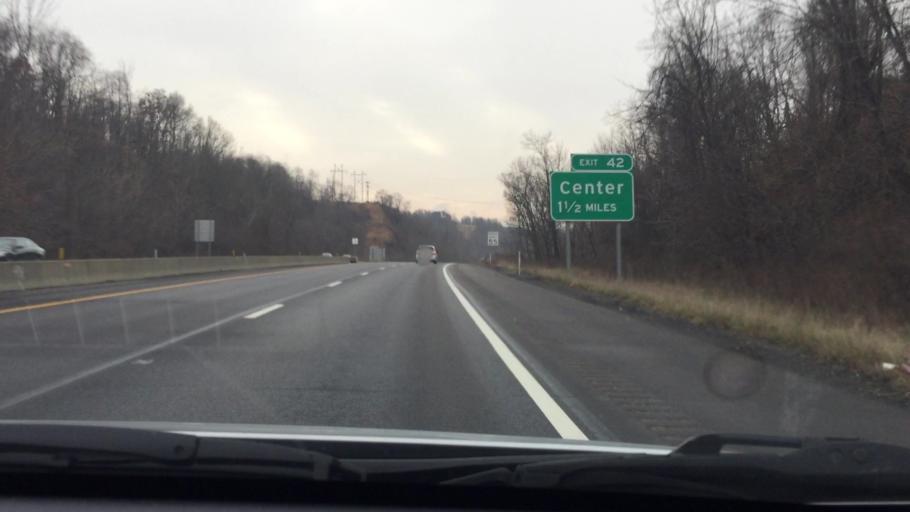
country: US
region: Pennsylvania
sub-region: Beaver County
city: Beaver
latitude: 40.6623
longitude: -80.3235
